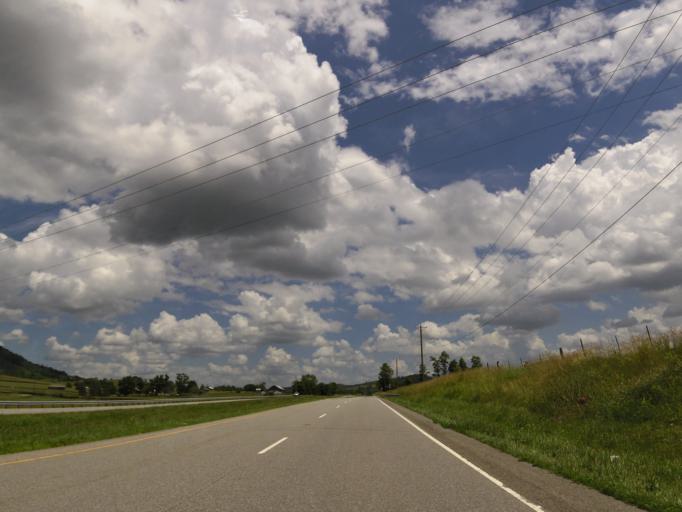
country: US
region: Tennessee
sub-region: Claiborne County
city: Harrogate
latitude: 36.6322
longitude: -83.4862
